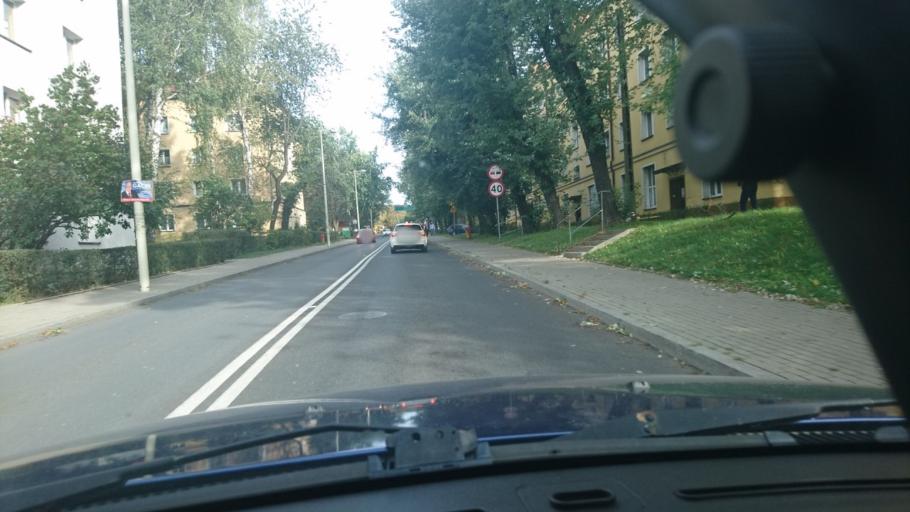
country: PL
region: Silesian Voivodeship
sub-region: Bielsko-Biala
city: Bielsko-Biala
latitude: 49.8157
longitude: 19.0531
